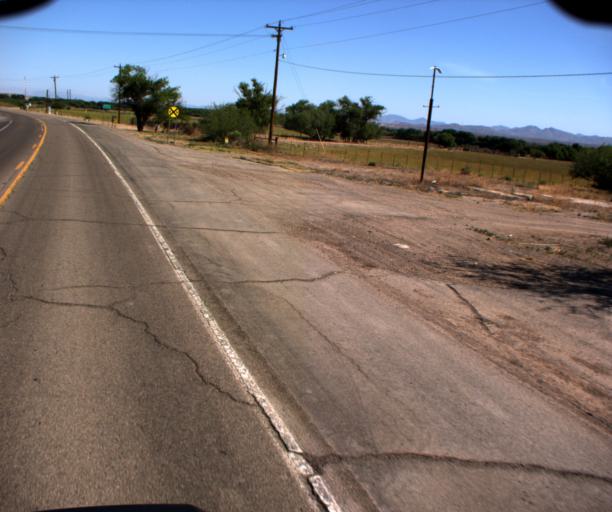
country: US
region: Arizona
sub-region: Greenlee County
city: Clifton
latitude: 32.7078
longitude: -109.0931
